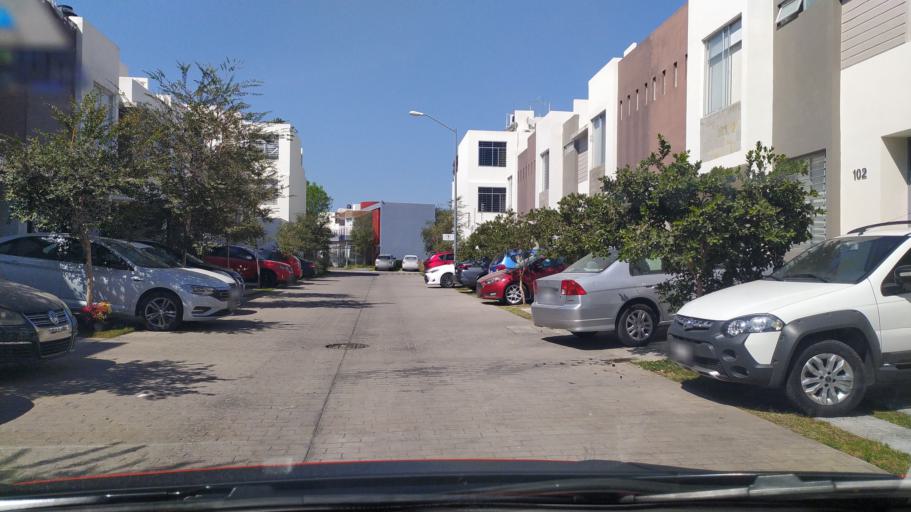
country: MX
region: Jalisco
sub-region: Tlajomulco de Zuniga
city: Palomar
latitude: 20.6300
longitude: -103.4635
